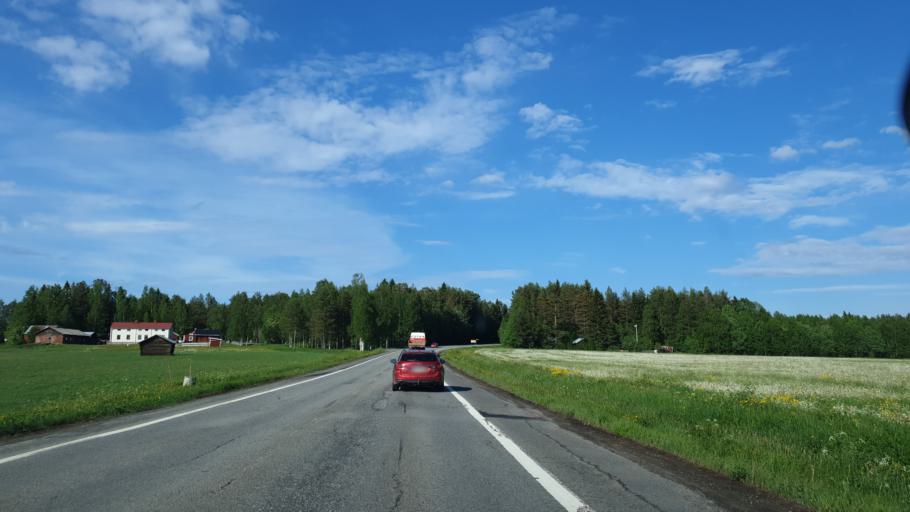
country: SE
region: Norrbotten
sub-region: Lulea Kommun
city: Gammelstad
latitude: 65.5920
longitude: 22.0397
